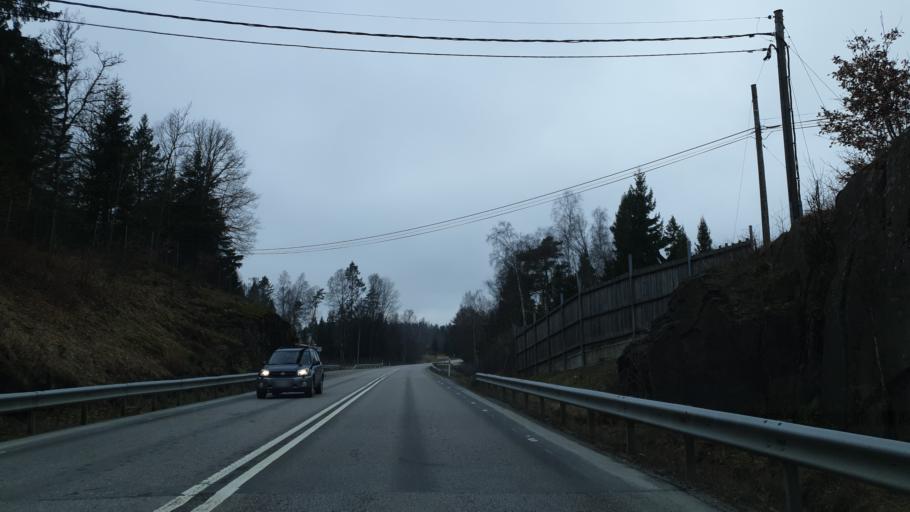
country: SE
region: Vaestra Goetaland
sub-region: Harryda Kommun
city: Hindas
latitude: 57.6535
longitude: 12.3887
